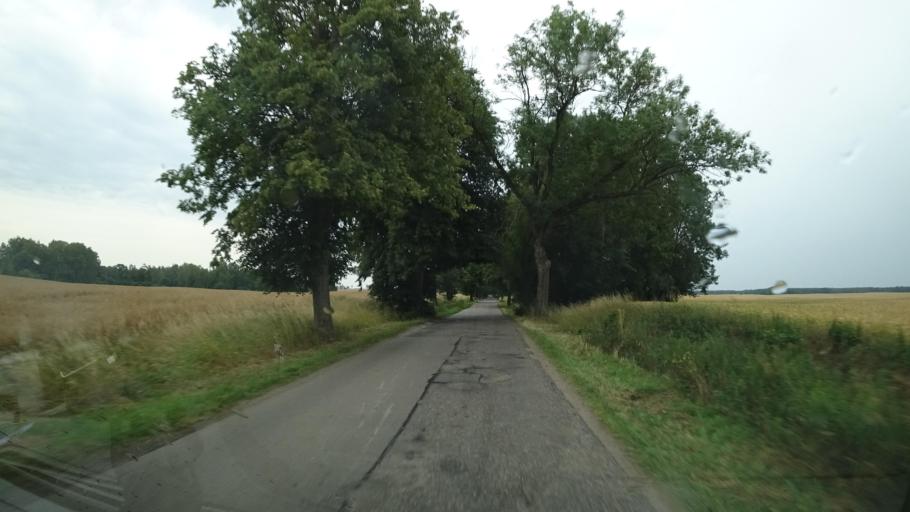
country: PL
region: Warmian-Masurian Voivodeship
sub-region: Powiat gizycki
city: Ryn
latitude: 53.9151
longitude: 21.5574
